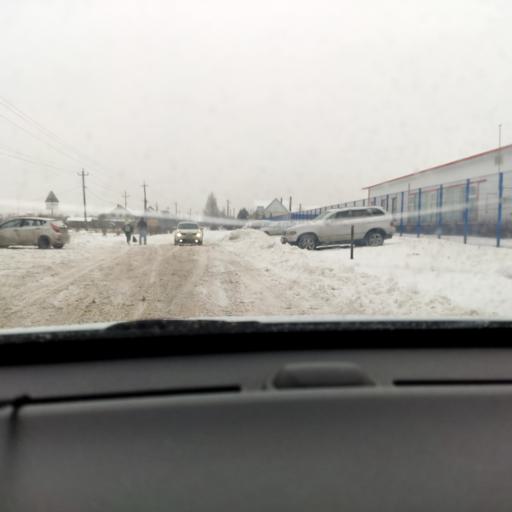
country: RU
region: Voronezj
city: Somovo
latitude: 51.6837
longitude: 39.3223
